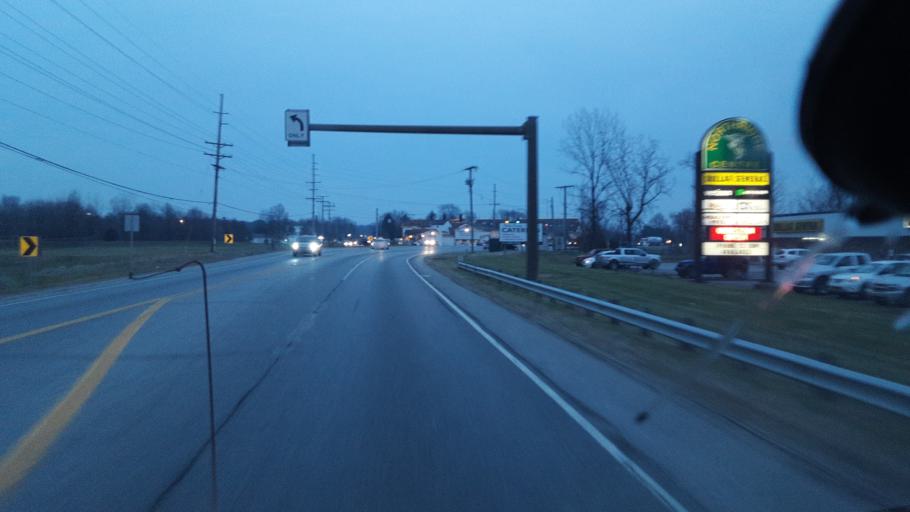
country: US
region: Indiana
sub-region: Elkhart County
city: Middlebury
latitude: 41.6683
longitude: -85.7296
